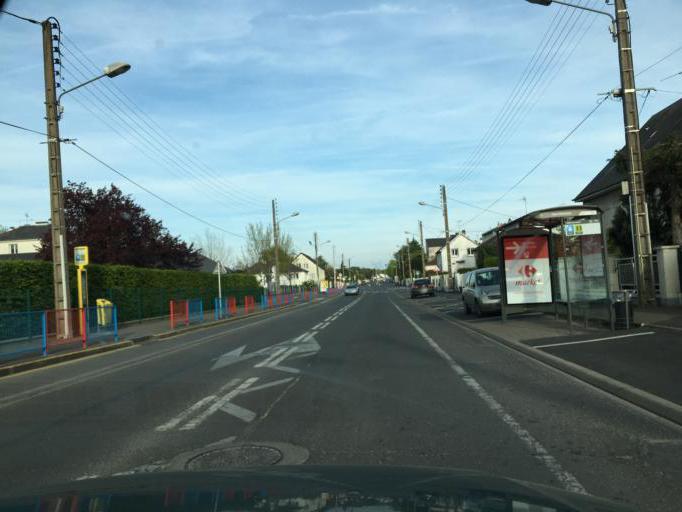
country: FR
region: Centre
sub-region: Departement du Loiret
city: Fleury-les-Aubrais
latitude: 47.9342
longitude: 1.9141
